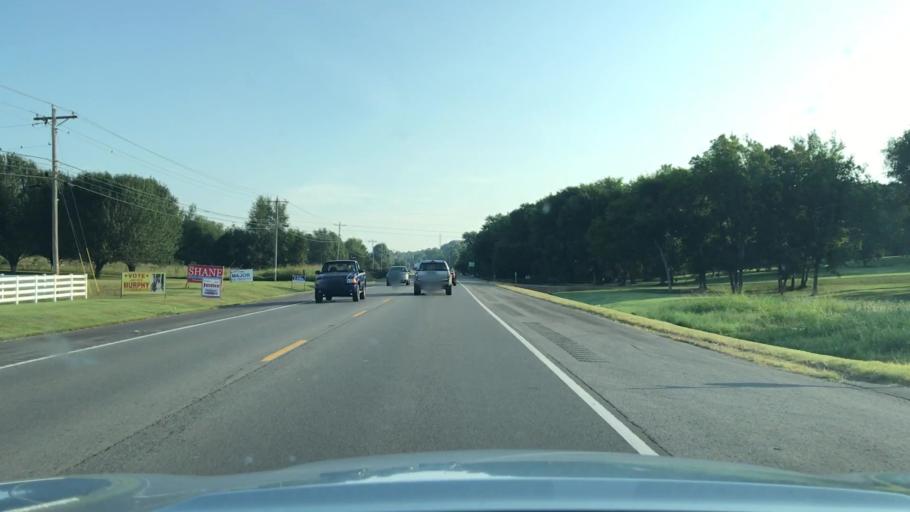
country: US
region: Tennessee
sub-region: Wilson County
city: Rural Hill
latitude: 36.1453
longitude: -86.5163
